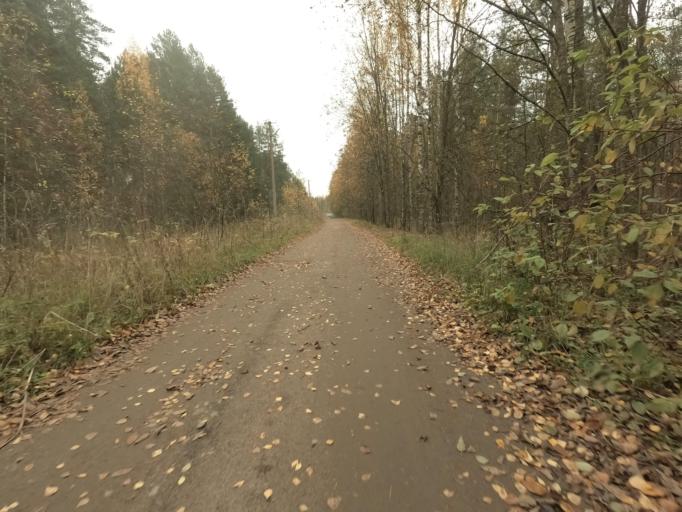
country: RU
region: Leningrad
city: Kirovsk
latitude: 59.8558
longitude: 30.9897
